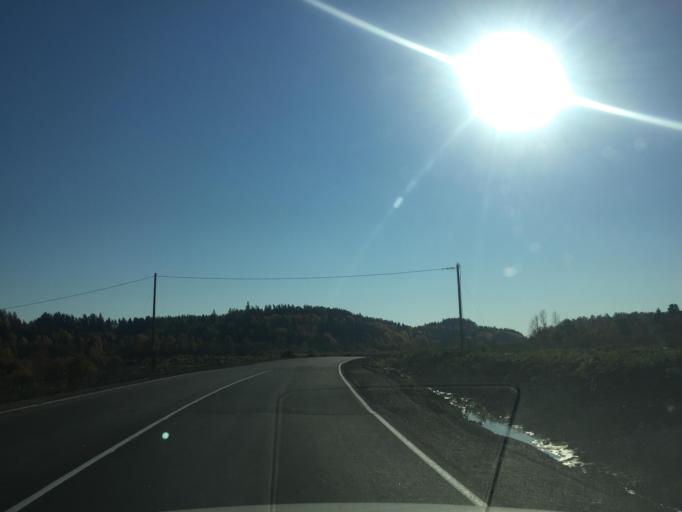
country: RU
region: Leningrad
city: Kuznechnoye
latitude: 61.3362
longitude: 29.8645
